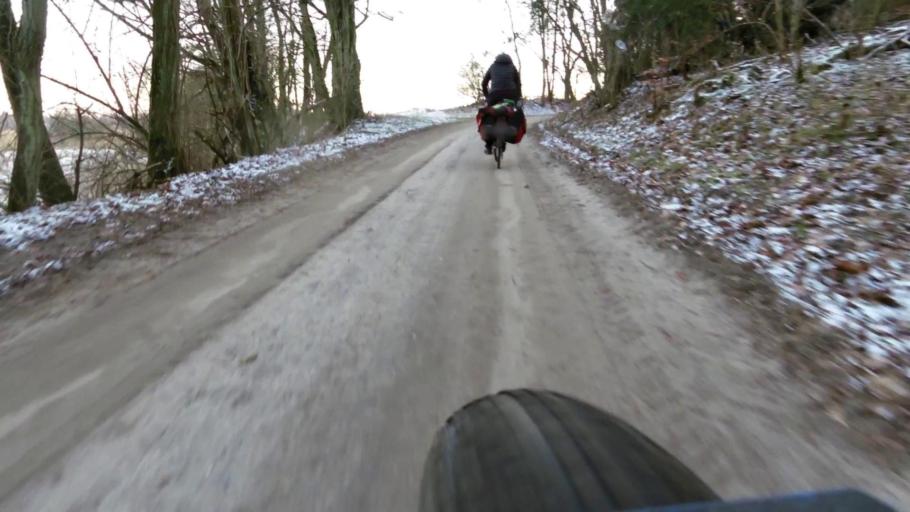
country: PL
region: West Pomeranian Voivodeship
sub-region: Powiat walecki
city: Walcz
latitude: 53.2483
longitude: 16.3726
